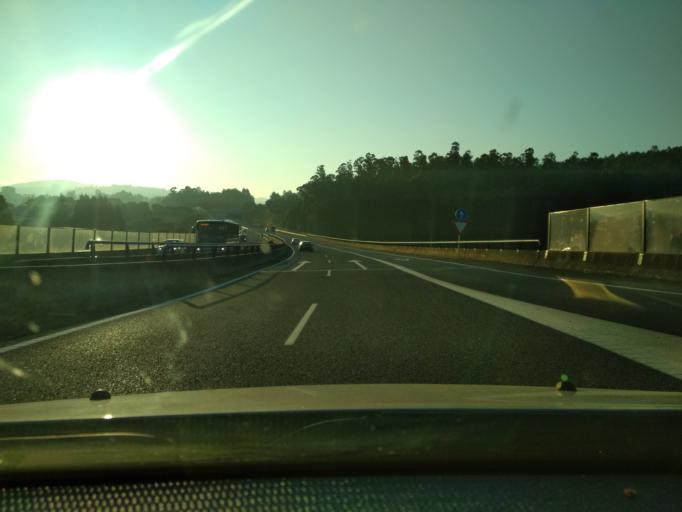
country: ES
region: Galicia
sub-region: Provincia da Coruna
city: Santiago de Compostela
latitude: 42.8560
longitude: -8.5735
